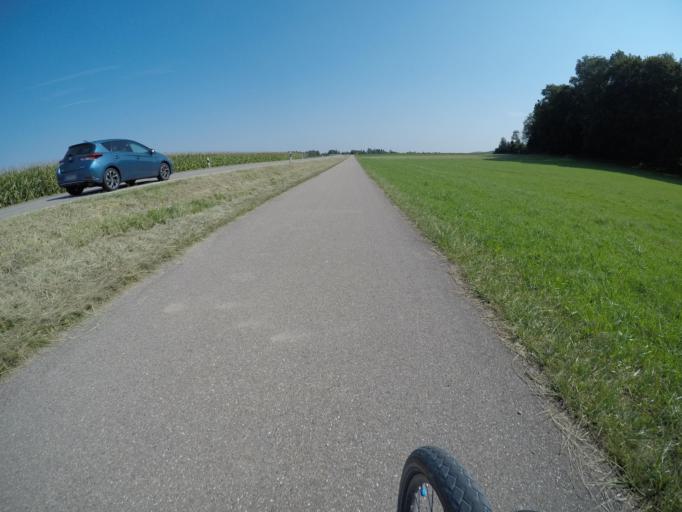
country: DE
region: Bavaria
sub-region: Swabia
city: Gundremmingen
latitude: 48.5092
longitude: 10.4203
